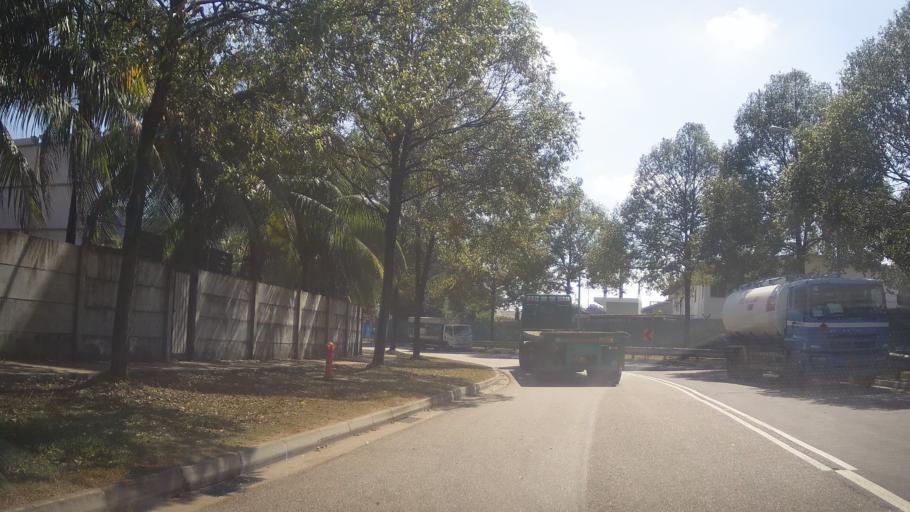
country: SG
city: Singapore
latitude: 1.3010
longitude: 103.6864
